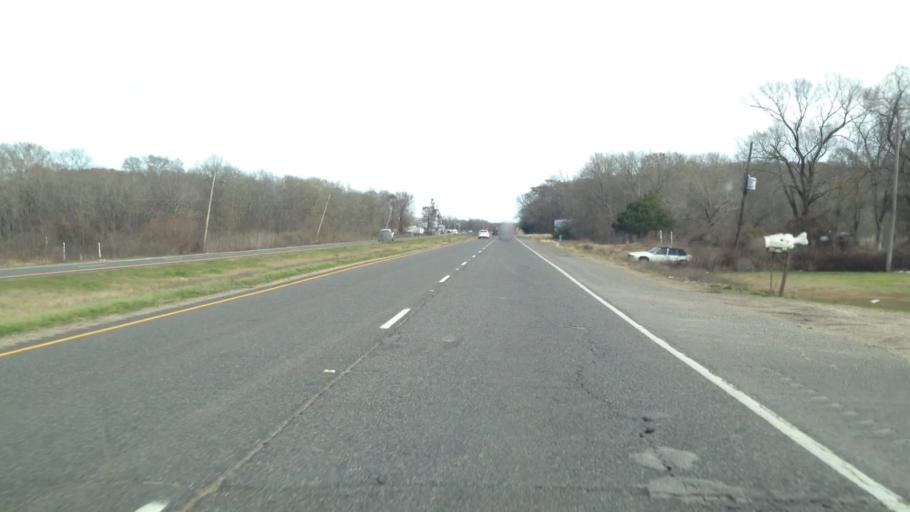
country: US
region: Louisiana
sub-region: Saint Landry Parish
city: Port Barre
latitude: 30.5476
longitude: -91.9966
